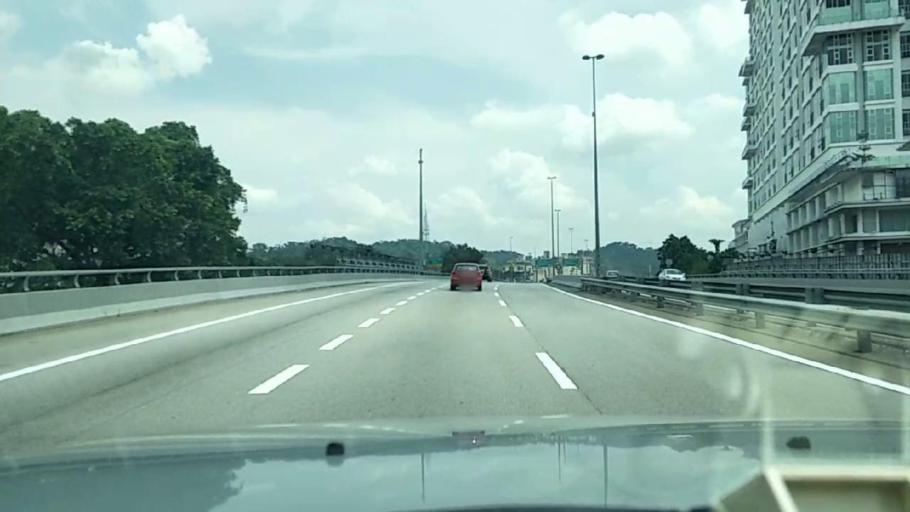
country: MY
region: Kuala Lumpur
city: Kuala Lumpur
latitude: 3.0939
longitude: 101.6758
